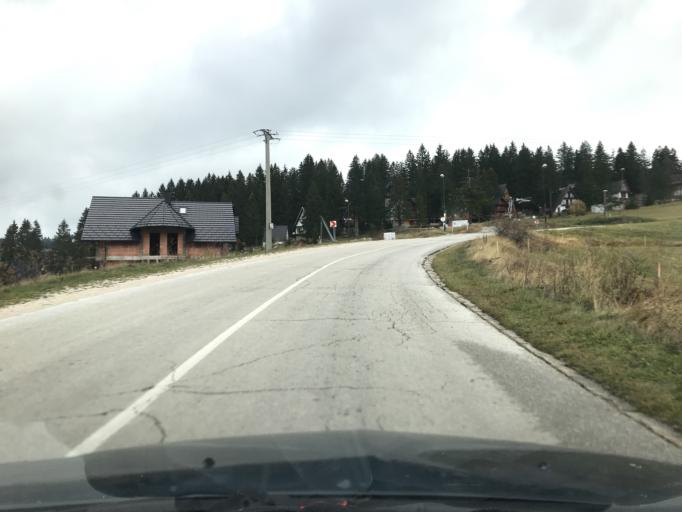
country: BA
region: Federation of Bosnia and Herzegovina
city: Turbe
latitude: 44.3145
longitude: 17.5662
